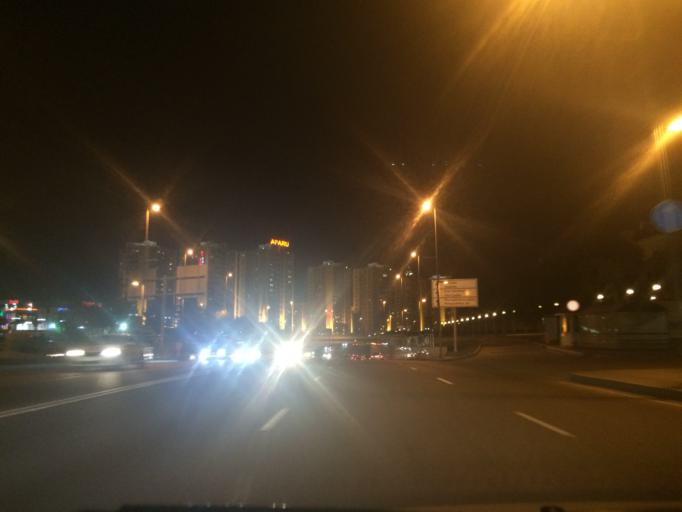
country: KZ
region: Astana Qalasy
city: Astana
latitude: 51.1530
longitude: 71.4337
